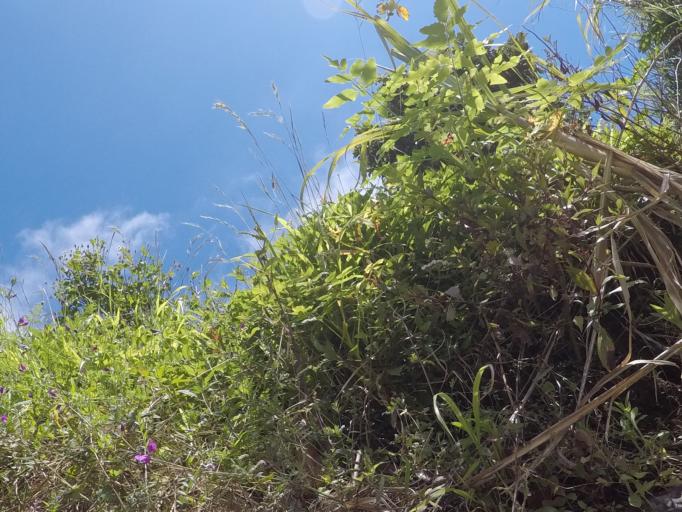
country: PT
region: Madeira
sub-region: Santana
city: Santana
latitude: 32.7726
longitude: -16.8781
